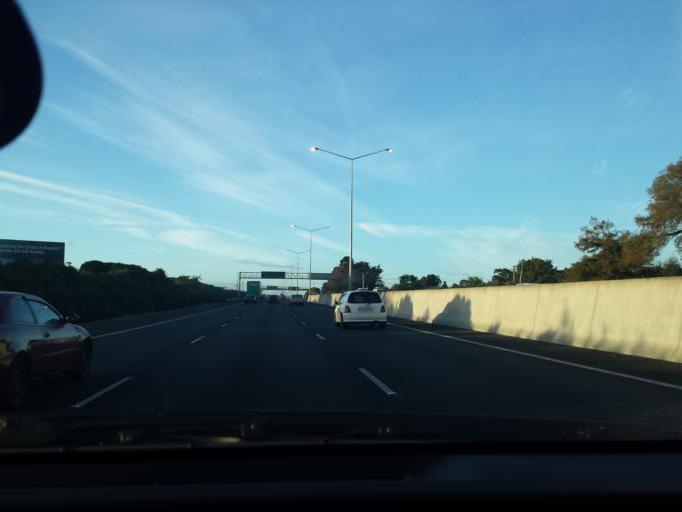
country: NZ
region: Auckland
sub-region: Auckland
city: Mangere
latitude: -36.9411
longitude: 174.7911
